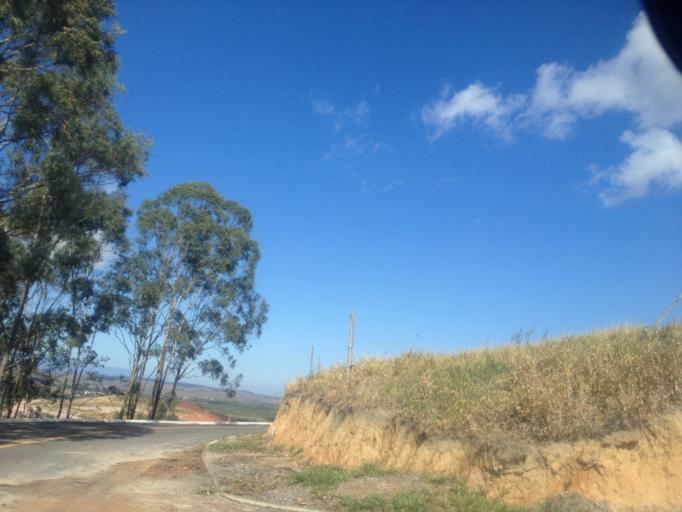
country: BR
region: Rio de Janeiro
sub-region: Porto Real
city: Porto Real
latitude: -22.4455
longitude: -44.3232
